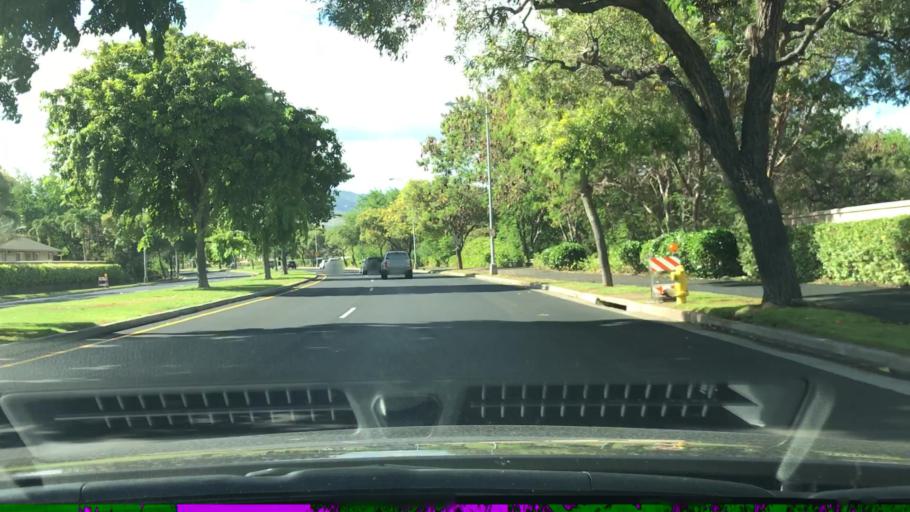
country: US
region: Hawaii
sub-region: Honolulu County
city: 'Ewa Gentry
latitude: 21.3353
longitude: -158.0295
